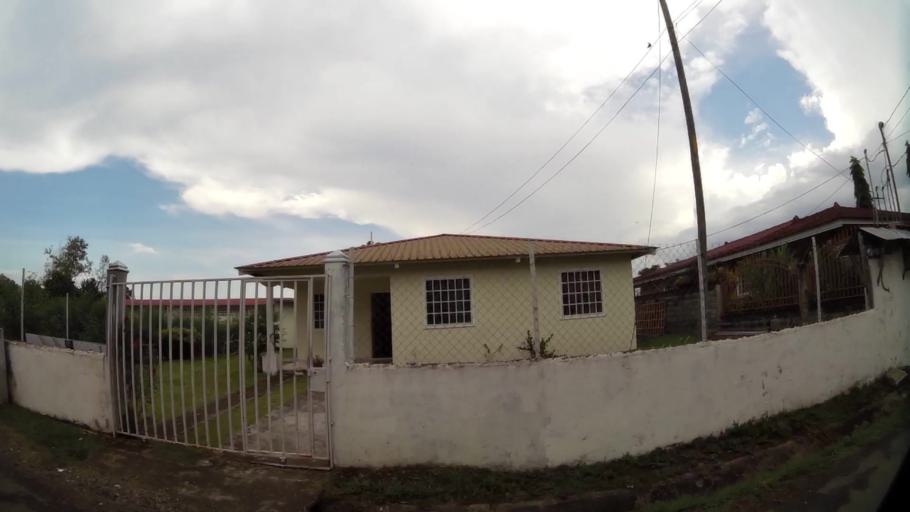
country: PA
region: Panama
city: Cabra Numero Uno
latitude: 9.1077
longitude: -79.3633
